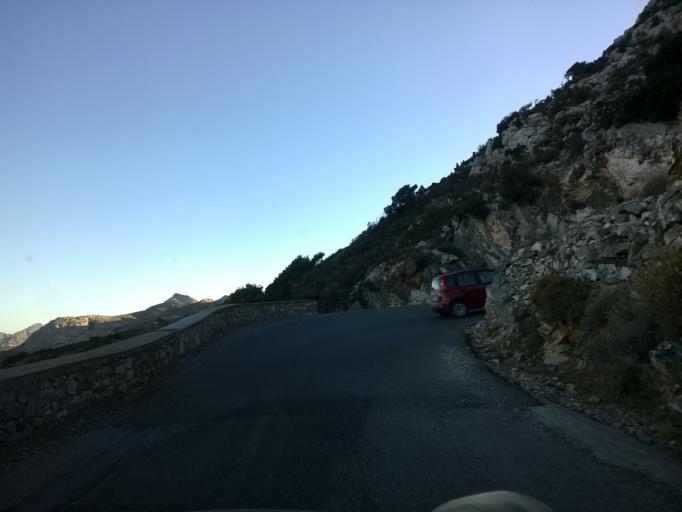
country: GR
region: South Aegean
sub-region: Nomos Kykladon
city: Filotion
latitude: 37.0469
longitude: 25.5057
